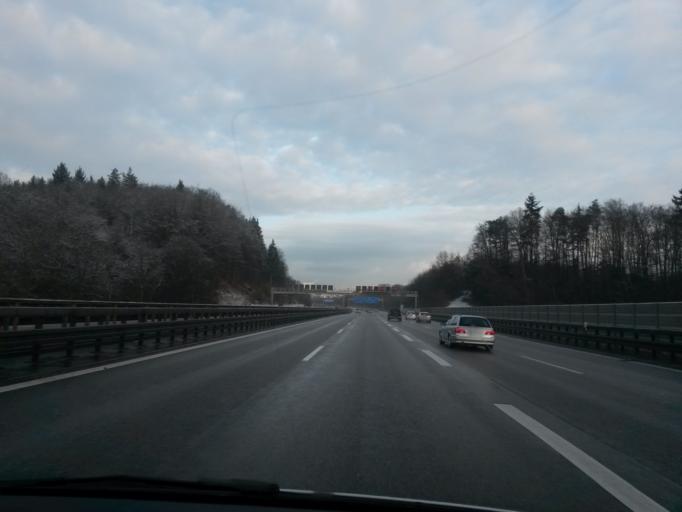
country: DE
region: Baden-Wuerttemberg
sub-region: Regierungsbezirk Stuttgart
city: Leonberg
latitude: 48.7666
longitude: 9.0314
